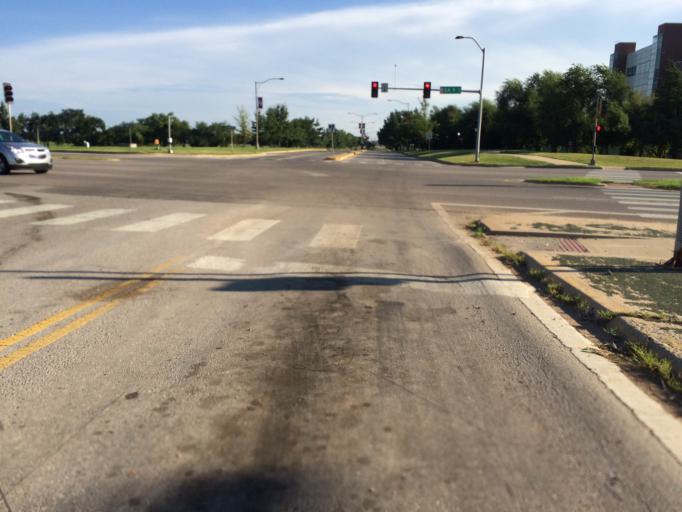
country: US
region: Oklahoma
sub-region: Cleveland County
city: Norman
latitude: 35.1802
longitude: -97.4413
